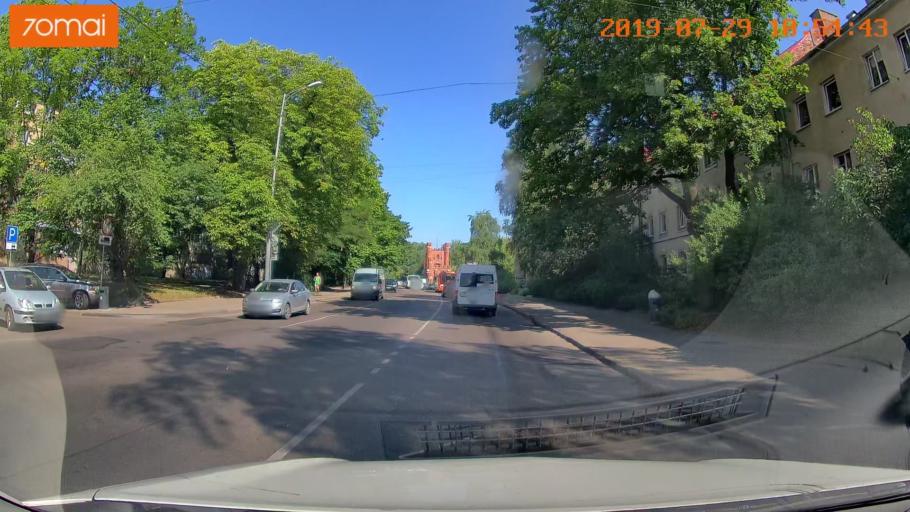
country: RU
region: Kaliningrad
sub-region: Gorod Kaliningrad
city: Kaliningrad
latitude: 54.7118
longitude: 20.5371
